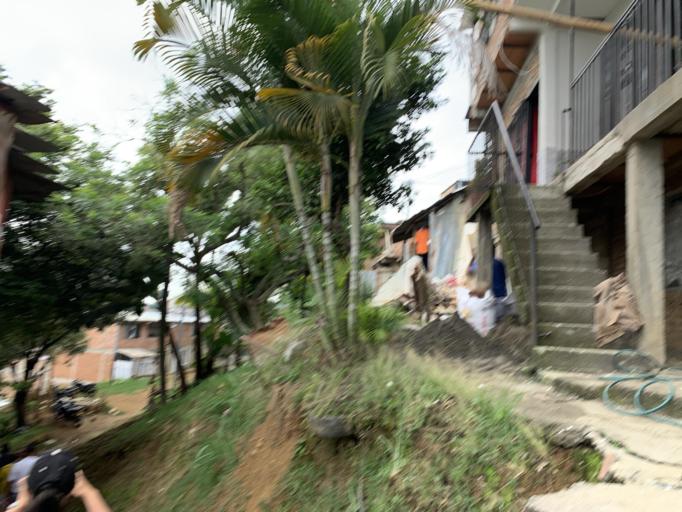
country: CO
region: Valle del Cauca
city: Cali
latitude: 3.3779
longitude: -76.5579
